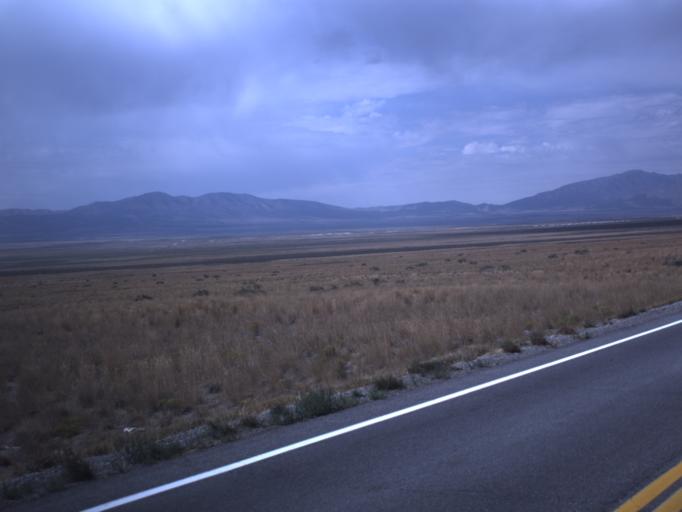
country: US
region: Utah
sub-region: Utah County
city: Eagle Mountain
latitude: 40.2650
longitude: -112.2370
